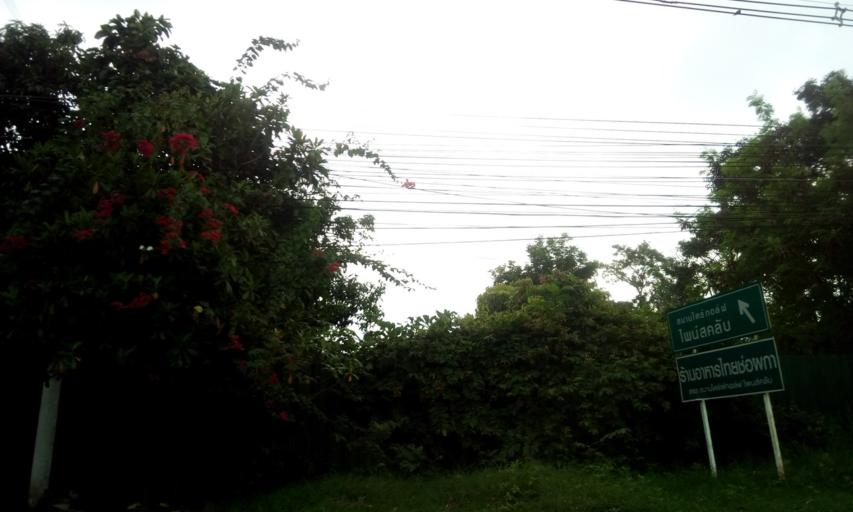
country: TH
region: Bangkok
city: Don Mueang
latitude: 13.9348
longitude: 100.5621
